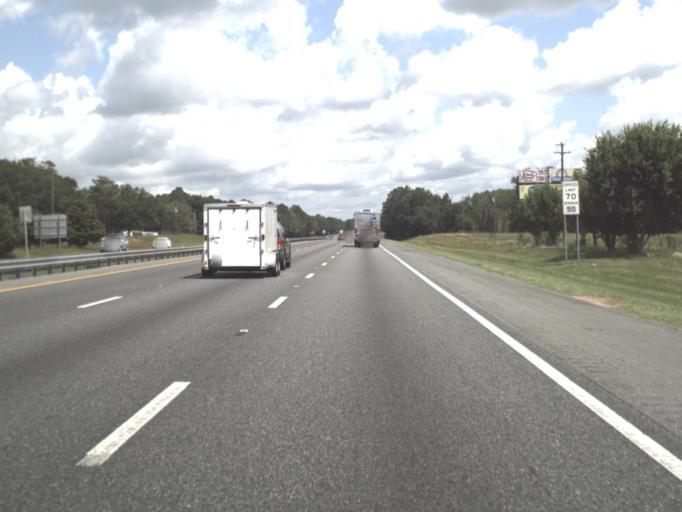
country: US
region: Florida
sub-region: Columbia County
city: Lake City
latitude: 30.1251
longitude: -82.6599
